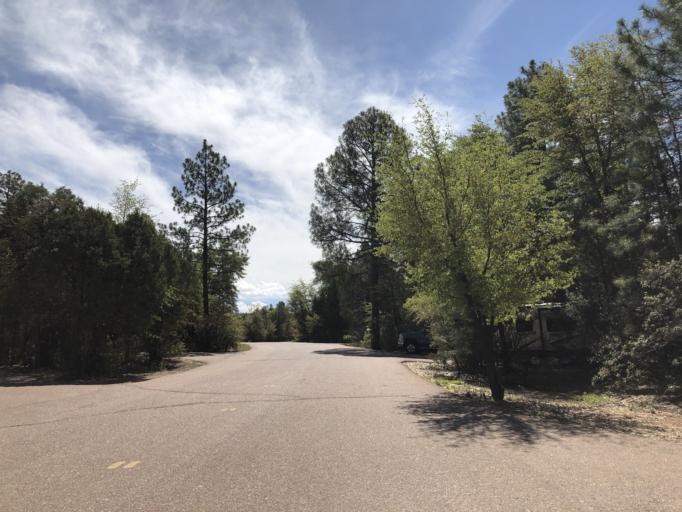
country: US
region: Arizona
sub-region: Gila County
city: Payson
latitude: 34.2727
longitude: -111.3177
